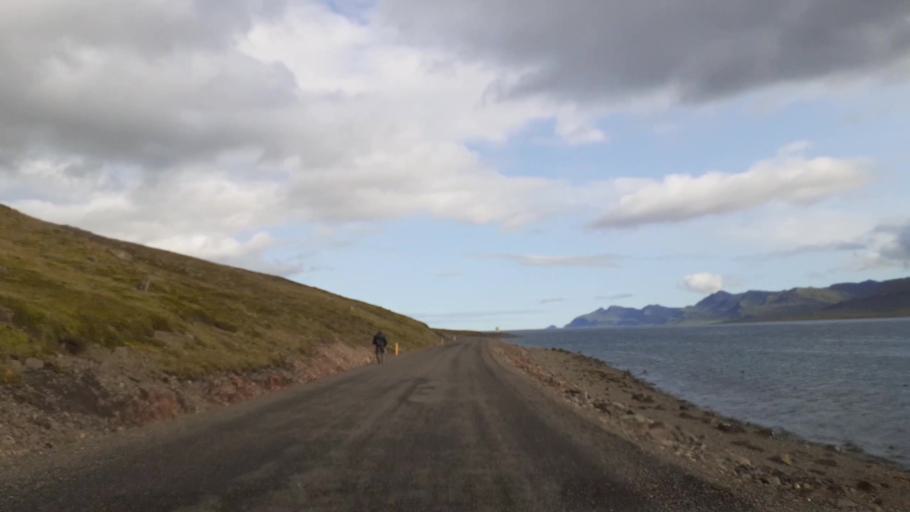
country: IS
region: East
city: Eskifjoerdur
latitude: 65.0596
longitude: -13.9899
